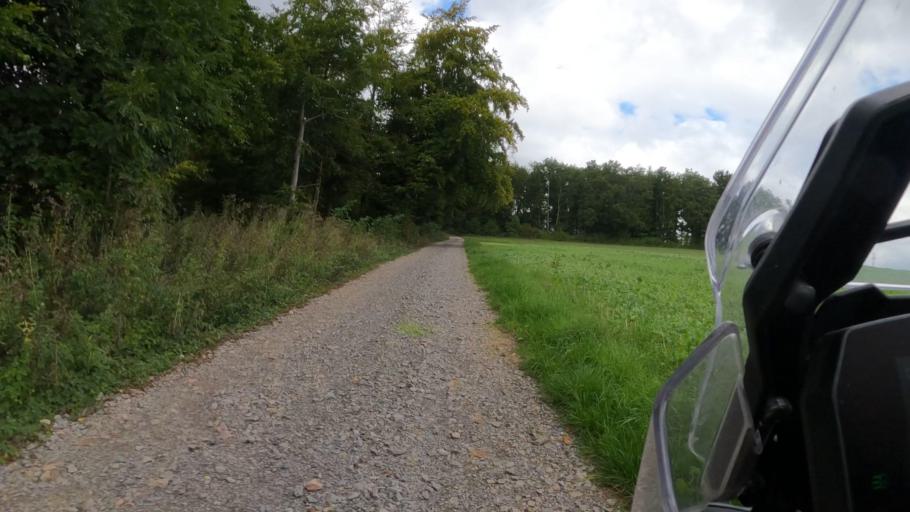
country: DE
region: Baden-Wuerttemberg
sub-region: Freiburg Region
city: Eggingen
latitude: 47.7061
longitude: 8.3652
